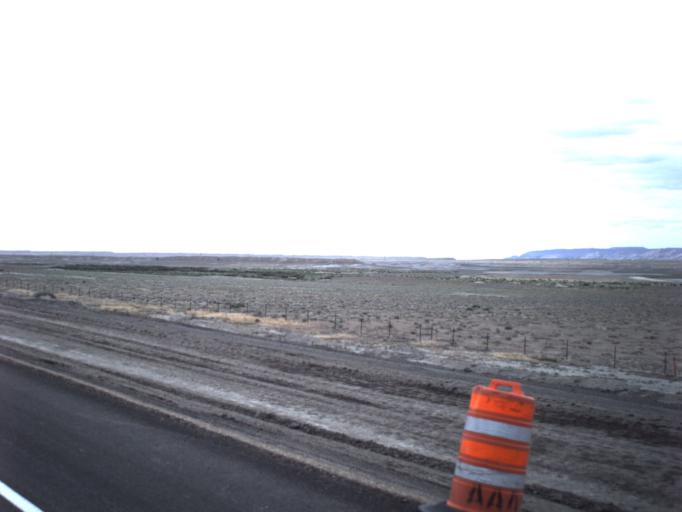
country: US
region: Utah
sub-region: Carbon County
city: East Carbon City
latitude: 39.0360
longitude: -110.3063
